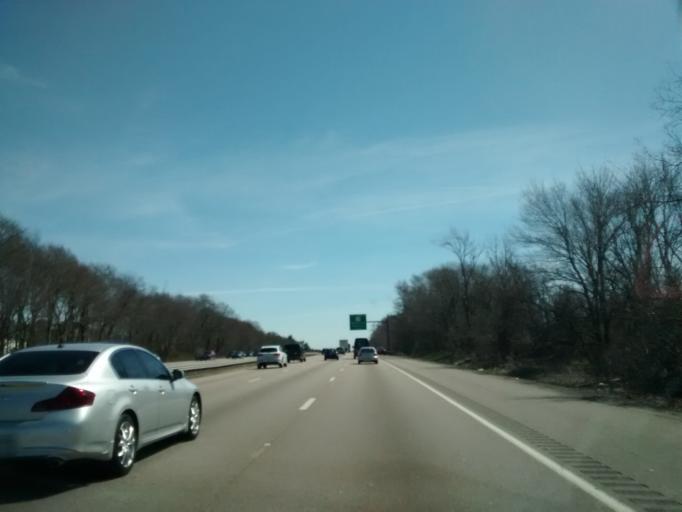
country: US
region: Massachusetts
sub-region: Norfolk County
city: Randolph
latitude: 42.1760
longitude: -71.0750
